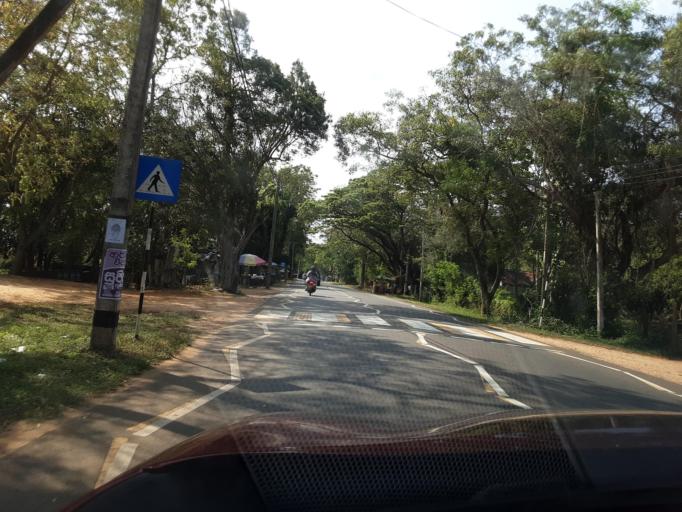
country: LK
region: Uva
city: Haputale
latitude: 6.3513
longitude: 81.1944
